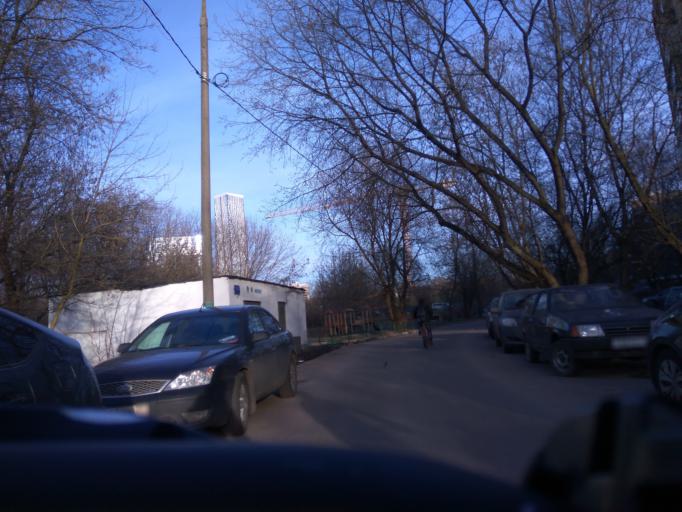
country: RU
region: Moskovskaya
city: Kastanayevo
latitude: 55.7235
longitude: 37.5139
